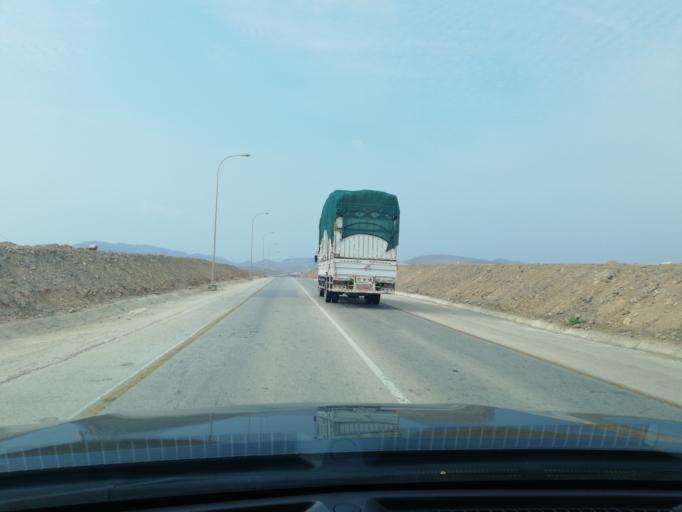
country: OM
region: Zufar
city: Salalah
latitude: 16.9286
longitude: 53.8429
